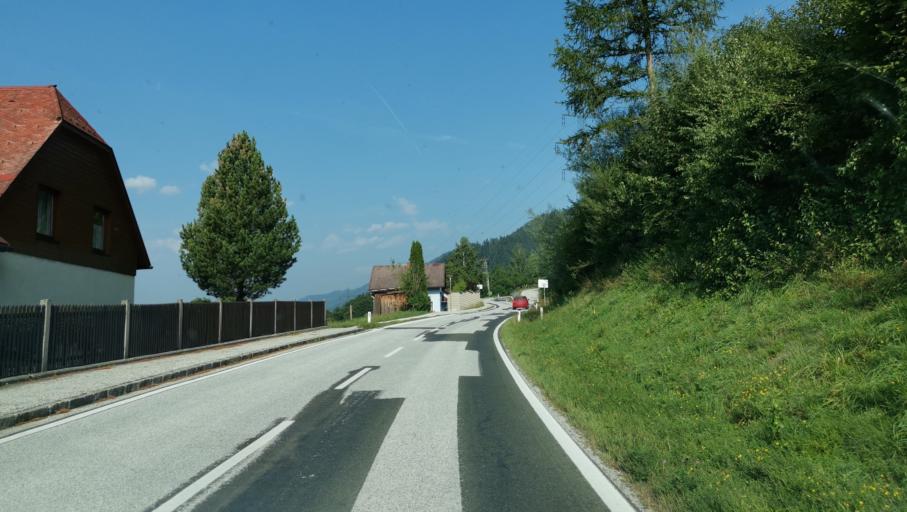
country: AT
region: Styria
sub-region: Politischer Bezirk Liezen
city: Trieben
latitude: 47.5072
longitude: 14.4707
